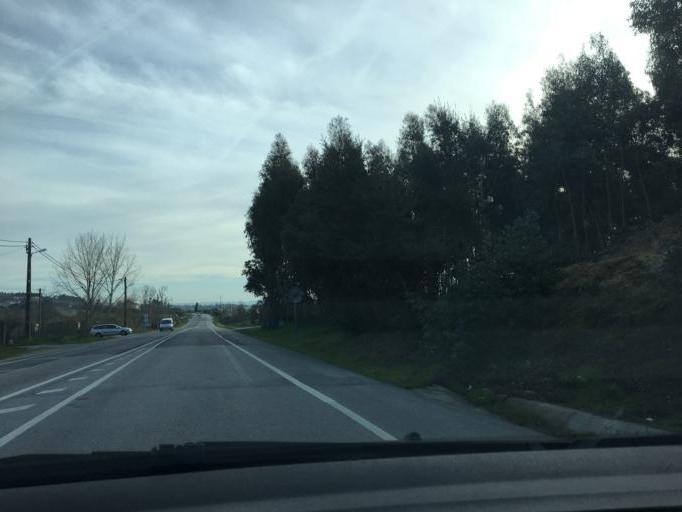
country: PT
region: Coimbra
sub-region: Soure
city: Alfarelos
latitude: 40.2006
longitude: -8.6418
